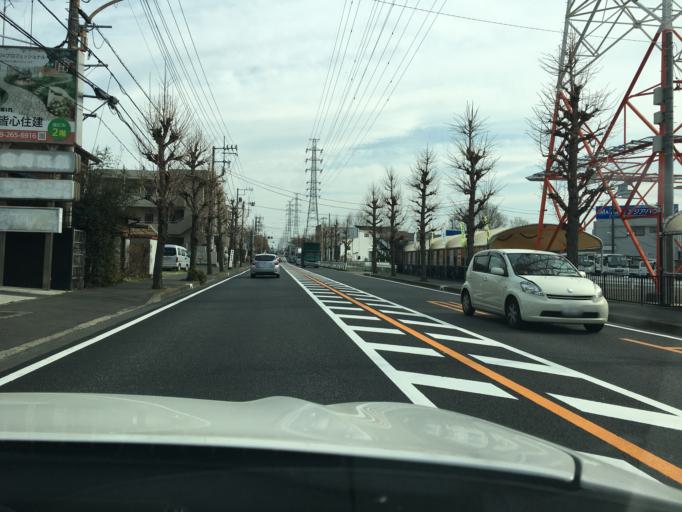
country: JP
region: Saitama
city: Kawagoe
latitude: 35.9097
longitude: 139.4709
